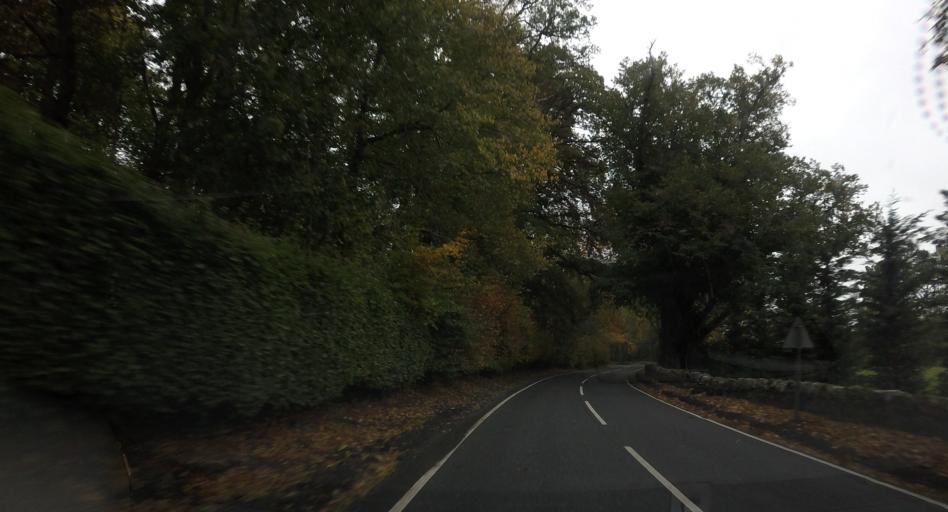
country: GB
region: Scotland
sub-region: Perth and Kinross
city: Bankfoot
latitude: 56.5482
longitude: -3.5140
